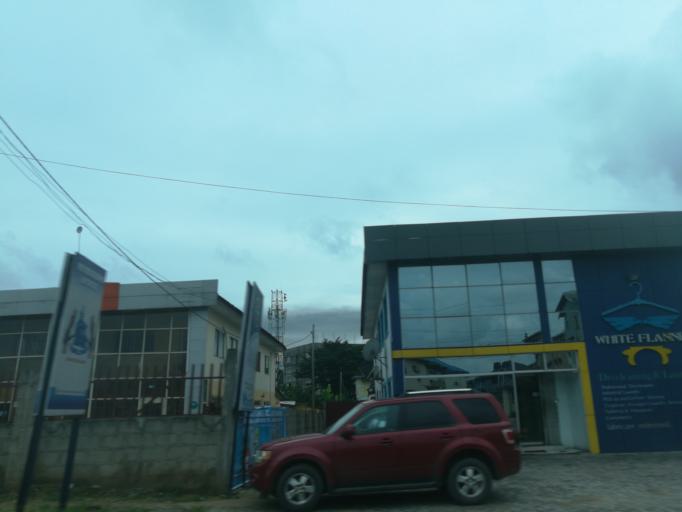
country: NG
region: Rivers
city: Port Harcourt
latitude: 4.8205
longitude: 6.9982
